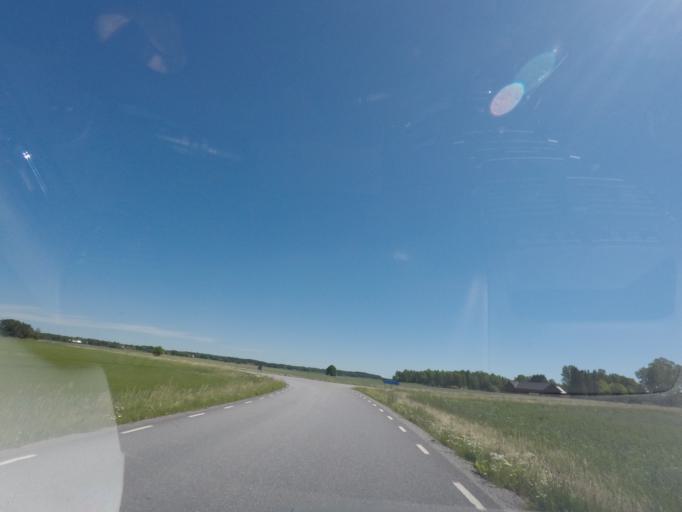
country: SE
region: Uppsala
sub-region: Enkopings Kommun
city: Enkoping
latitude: 59.7068
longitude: 17.0390
